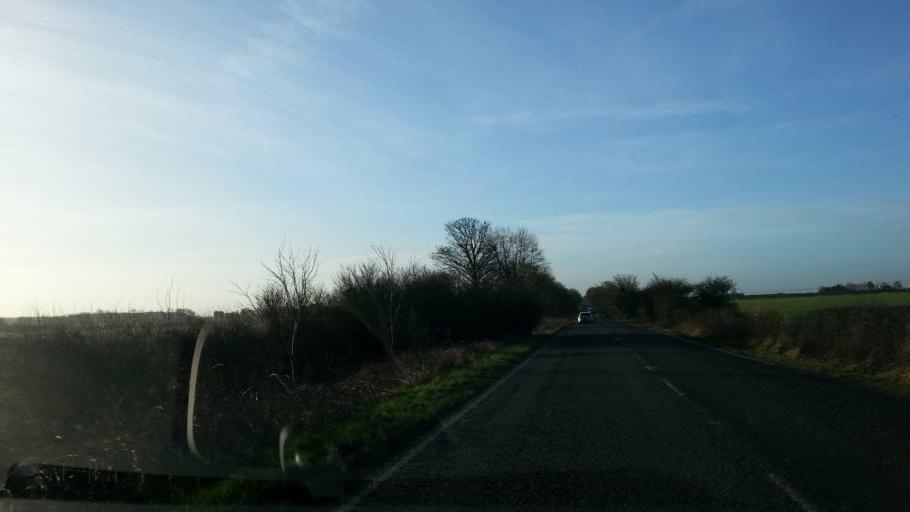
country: GB
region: England
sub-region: Lincolnshire
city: Grantham
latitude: 52.9233
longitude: -0.5743
